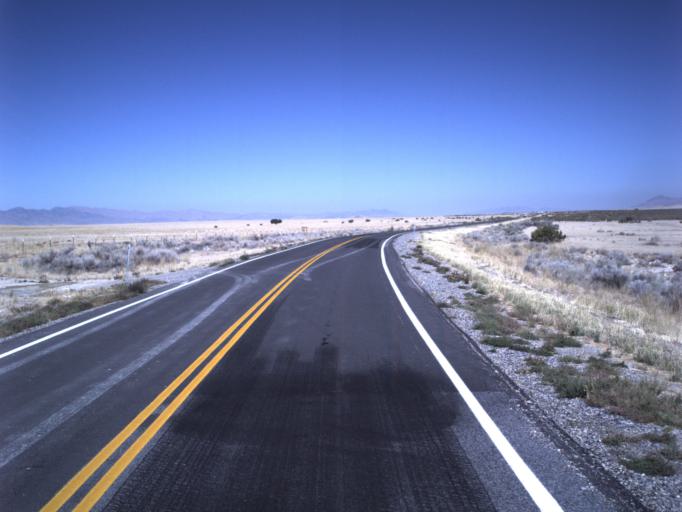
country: US
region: Utah
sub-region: Tooele County
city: Grantsville
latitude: 40.2569
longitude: -112.7403
